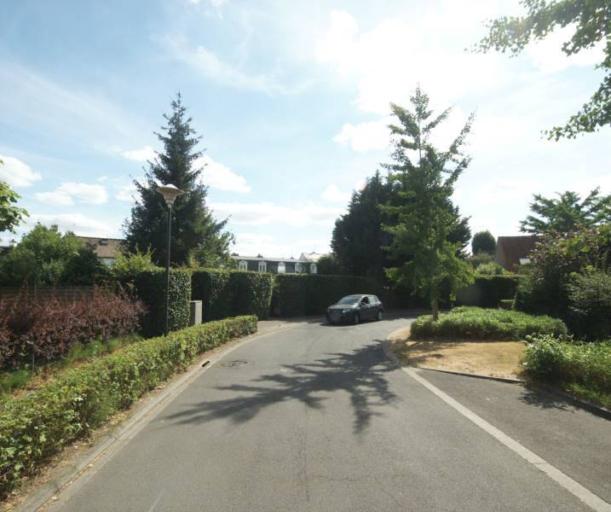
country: FR
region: Nord-Pas-de-Calais
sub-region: Departement du Nord
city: Bondues
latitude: 50.6831
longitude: 3.0933
